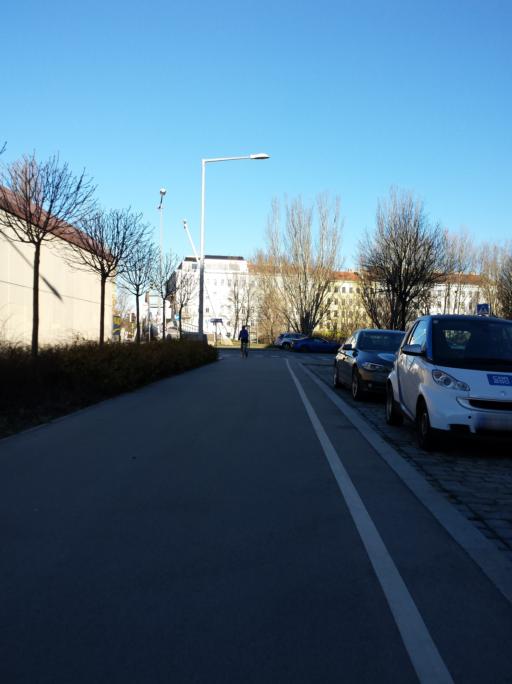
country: AT
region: Vienna
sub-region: Wien Stadt
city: Vienna
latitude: 48.2015
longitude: 16.4017
